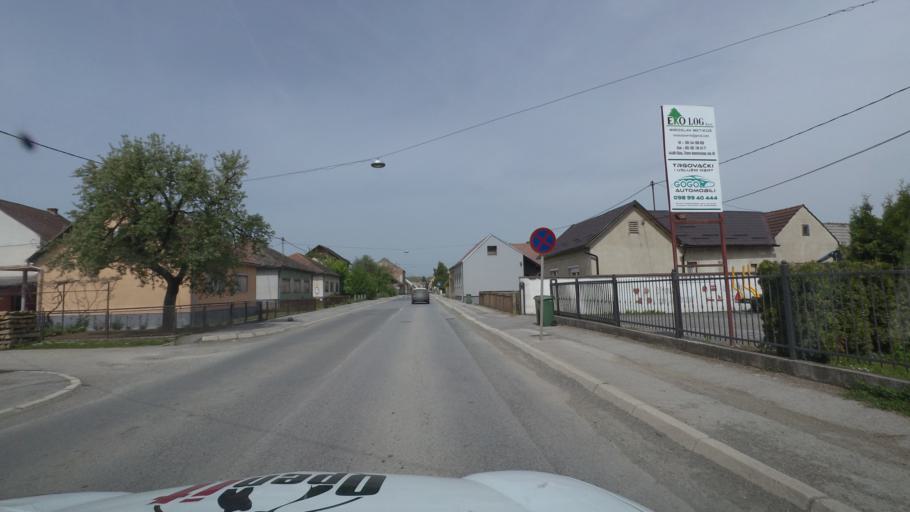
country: HR
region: Sisacko-Moslavacka
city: Glina
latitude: 45.3348
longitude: 16.0963
